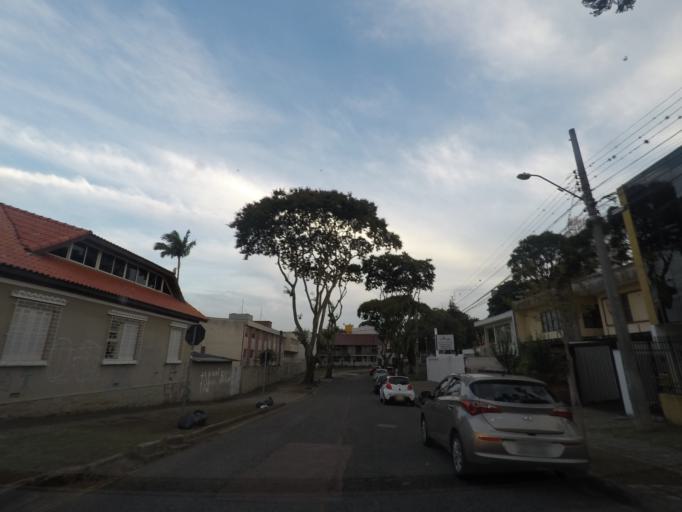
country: BR
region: Parana
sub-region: Curitiba
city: Curitiba
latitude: -25.4216
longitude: -49.2778
